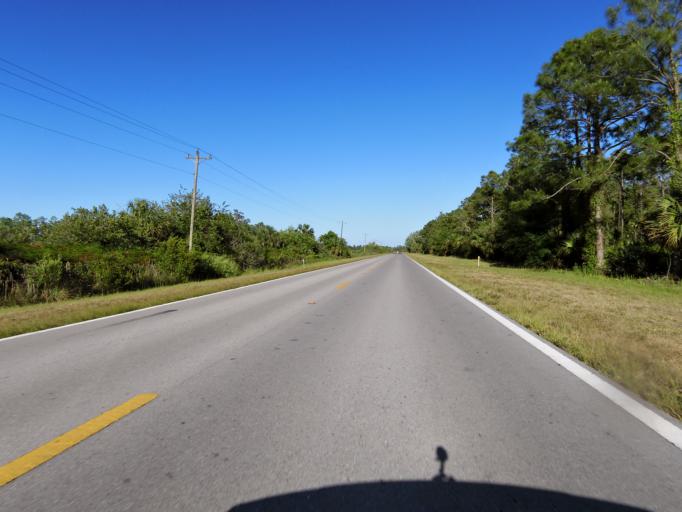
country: US
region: Florida
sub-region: Collier County
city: Immokalee
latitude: 26.2954
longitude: -81.3782
